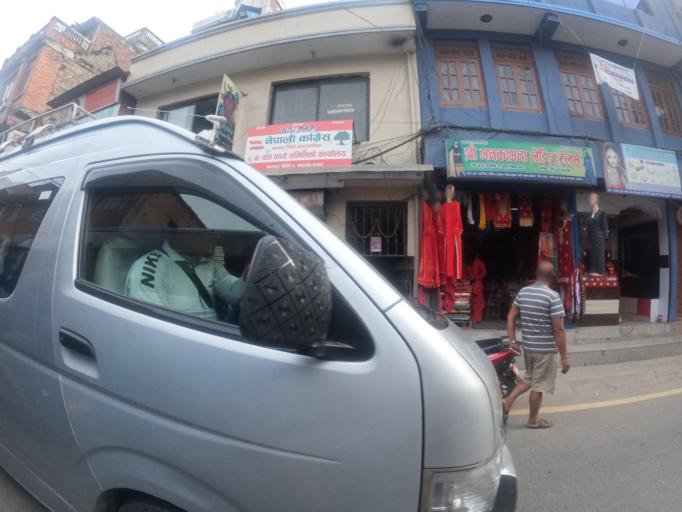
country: NP
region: Central Region
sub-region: Bagmati Zone
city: Bhaktapur
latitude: 27.6831
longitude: 85.3879
